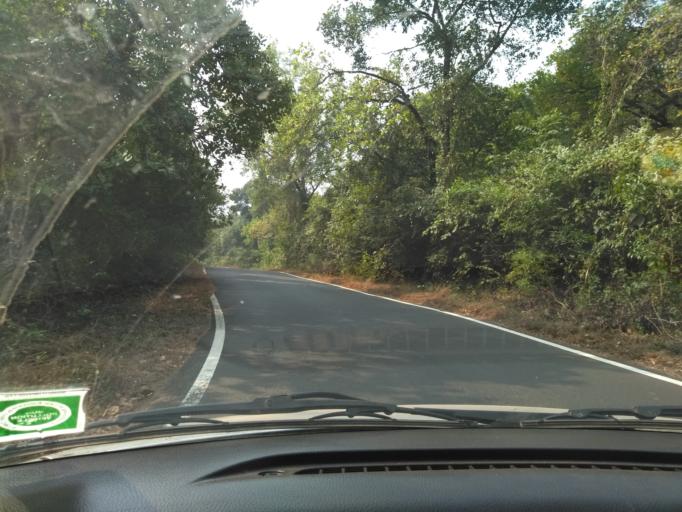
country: IN
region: Goa
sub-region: North Goa
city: Pernem
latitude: 15.7731
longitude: 73.9203
